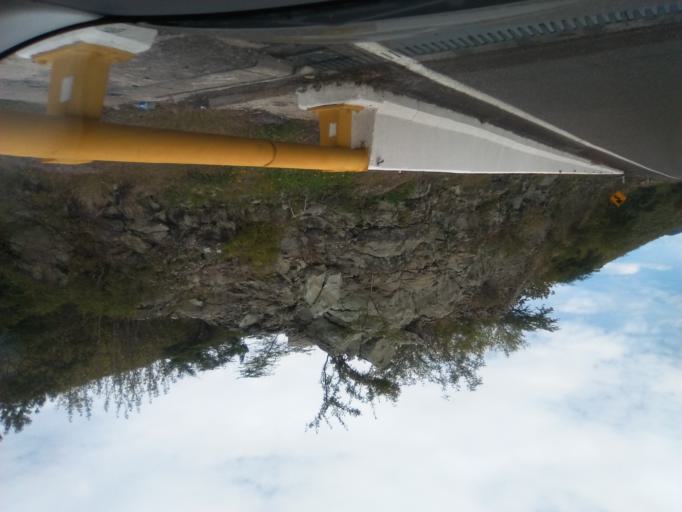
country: MX
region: Guerrero
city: Zumpango del Rio
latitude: 17.6984
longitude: -99.5075
